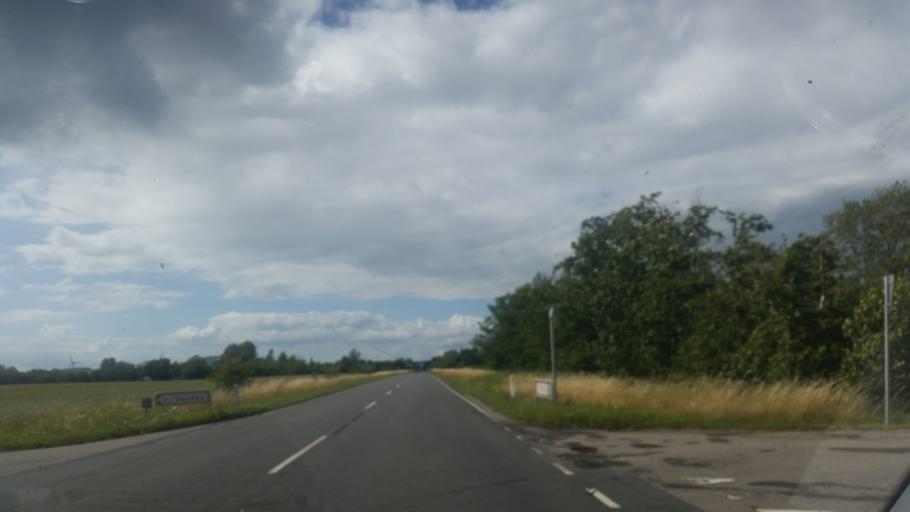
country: DK
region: Zealand
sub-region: Odsherred Kommune
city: Asnaes
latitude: 55.7626
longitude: 11.5048
